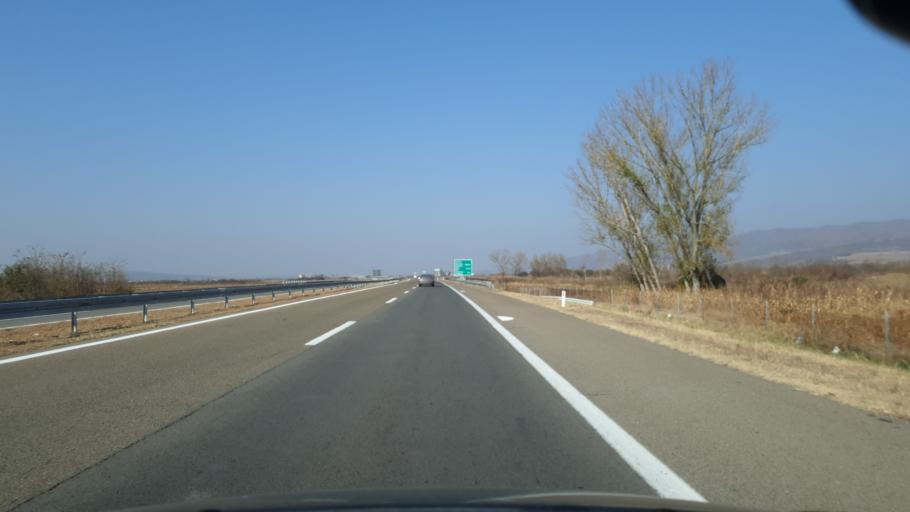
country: RS
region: Central Serbia
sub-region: Nisavski Okrug
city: Doljevac
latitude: 43.1578
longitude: 21.8894
